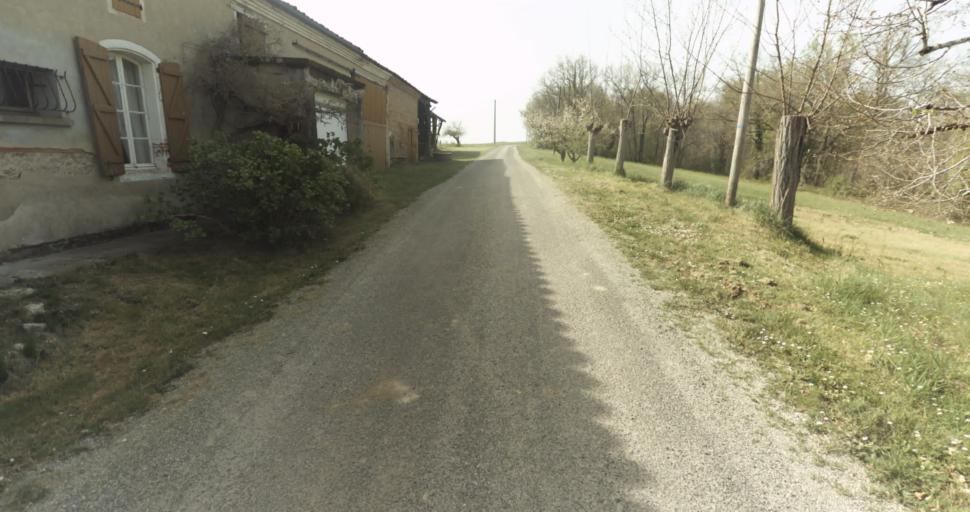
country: FR
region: Midi-Pyrenees
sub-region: Departement du Tarn-et-Garonne
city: Lafrancaise
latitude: 44.1537
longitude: 1.1741
